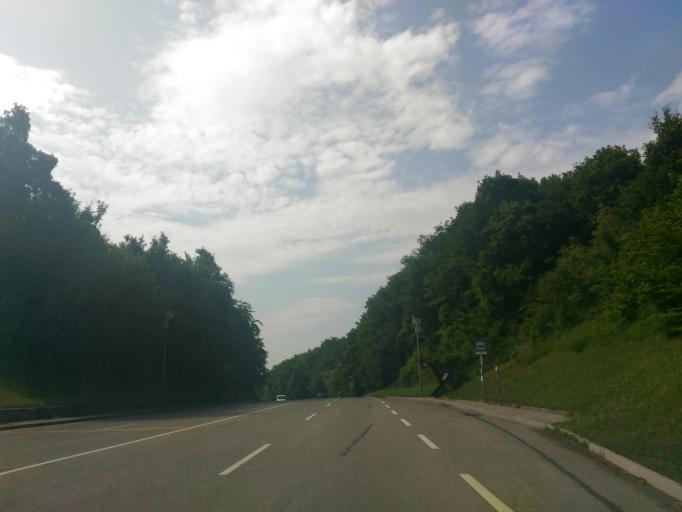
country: HU
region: Baranya
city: Pecs
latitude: 46.1373
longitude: 18.2505
